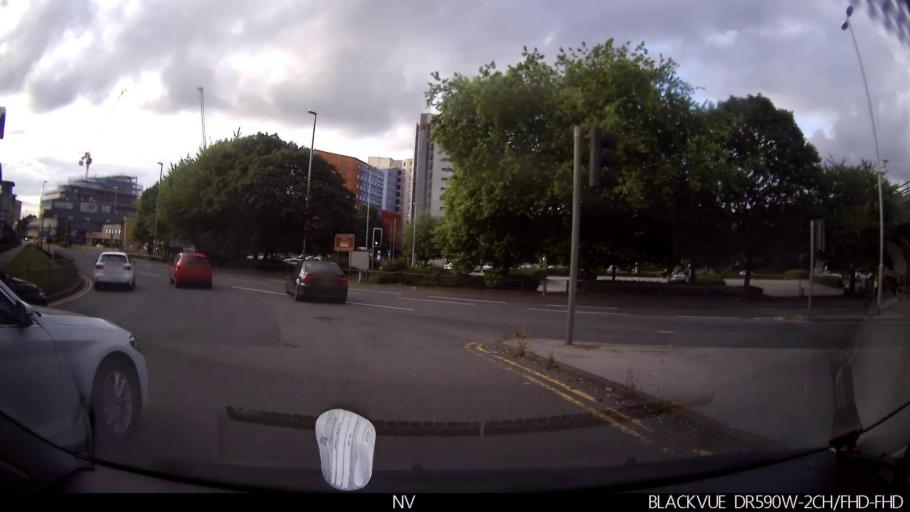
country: GB
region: England
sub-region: City and Borough of Leeds
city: Leeds
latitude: 53.7975
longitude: -1.5611
